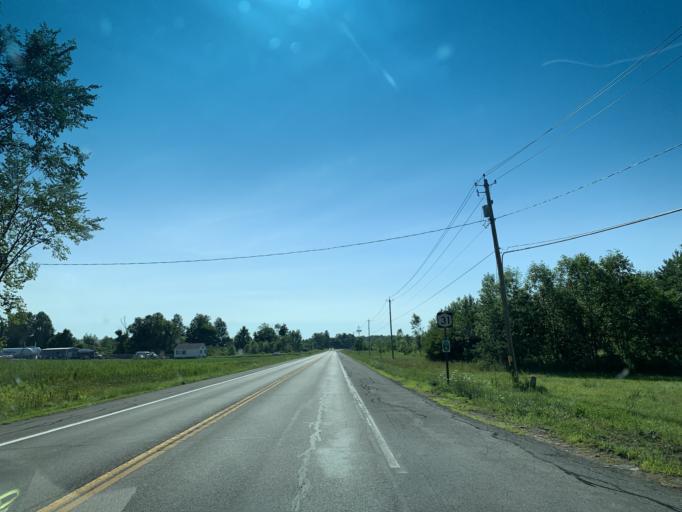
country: US
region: New York
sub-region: Oneida County
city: Sherrill
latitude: 43.1349
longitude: -75.5981
